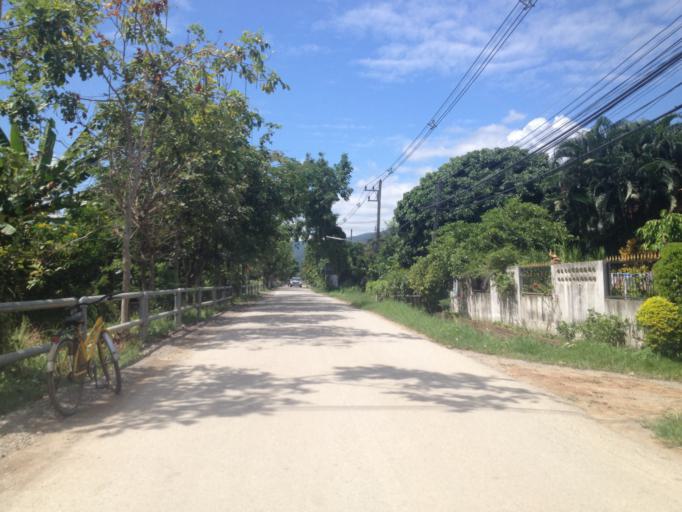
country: TH
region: Chiang Mai
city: Chiang Mai
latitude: 18.7596
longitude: 98.9576
